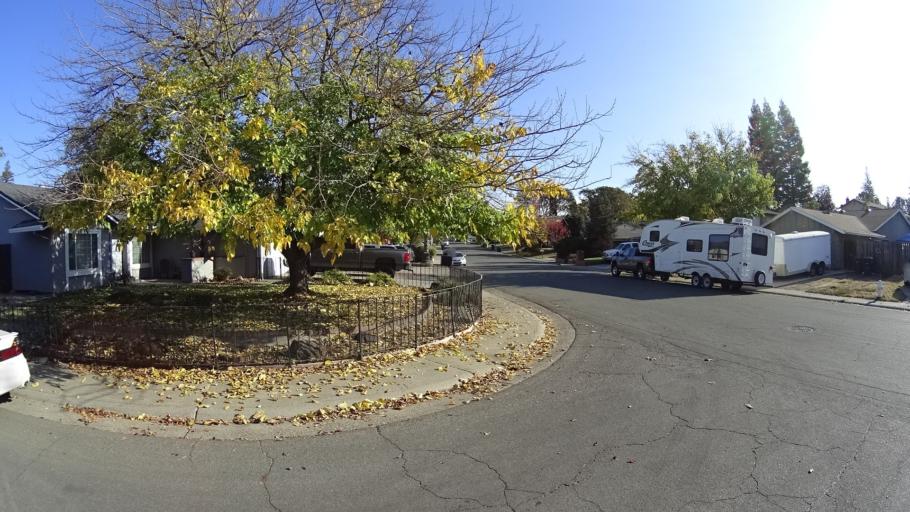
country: US
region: California
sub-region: Sacramento County
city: Citrus Heights
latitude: 38.7143
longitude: -121.2595
